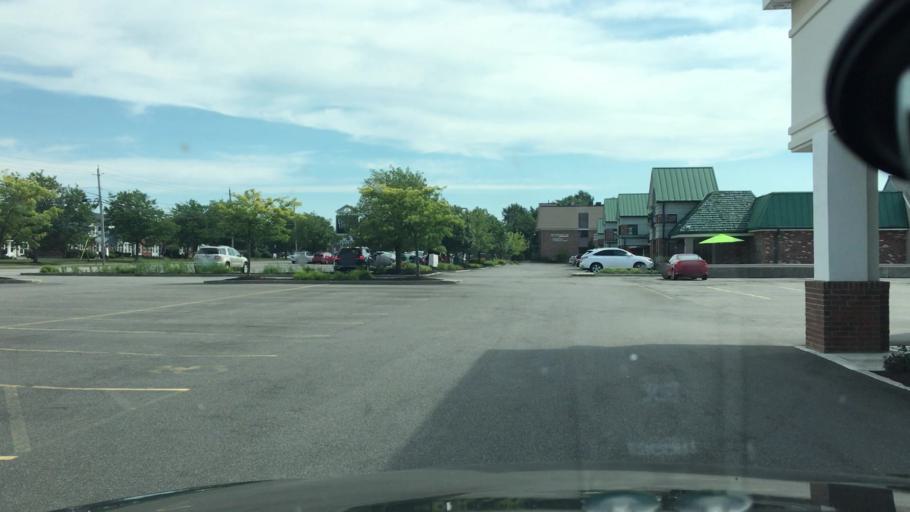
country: US
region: New York
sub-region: Erie County
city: Williamsville
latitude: 42.9762
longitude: -78.7402
